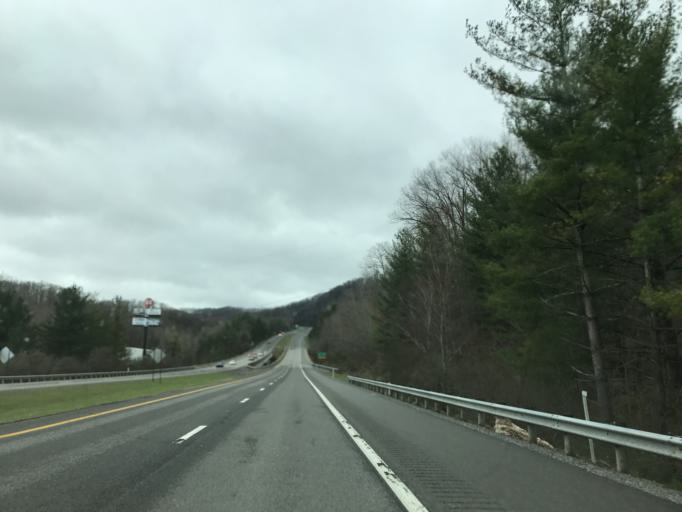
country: US
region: West Virginia
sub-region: Fayette County
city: Mount Hope
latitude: 37.8978
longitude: -81.1803
